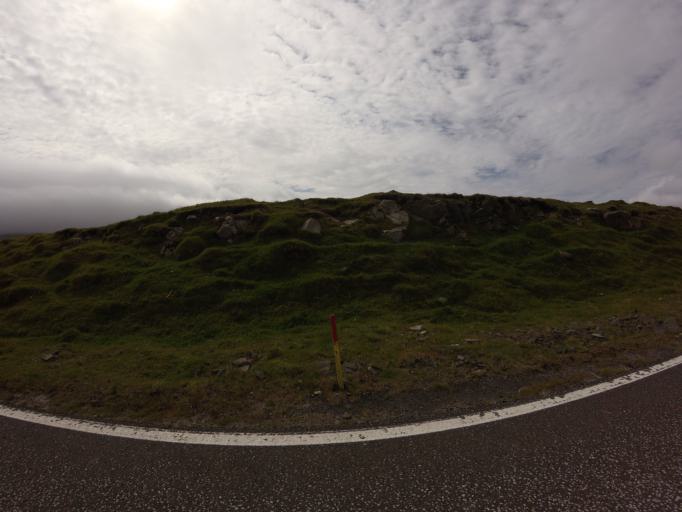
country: FO
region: Sandoy
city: Sandur
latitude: 61.8290
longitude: -6.7595
